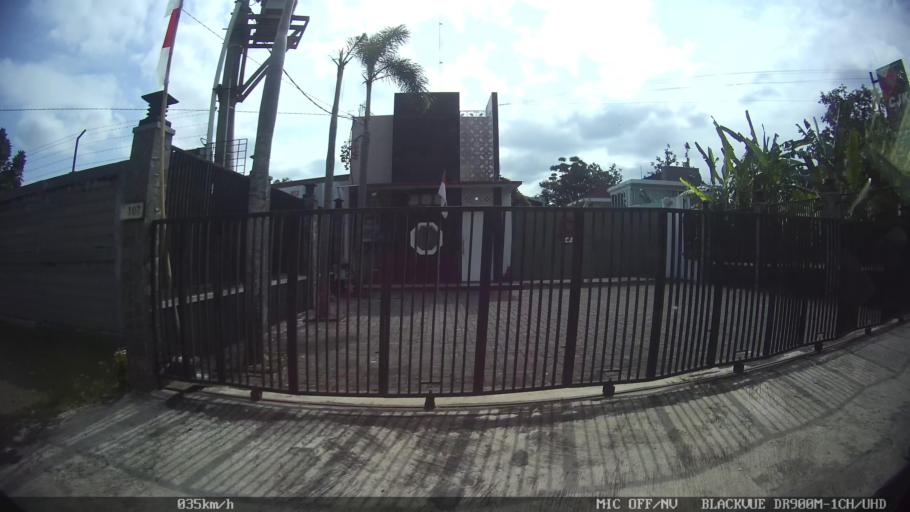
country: ID
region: Daerah Istimewa Yogyakarta
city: Depok
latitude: -7.7603
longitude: 110.4188
